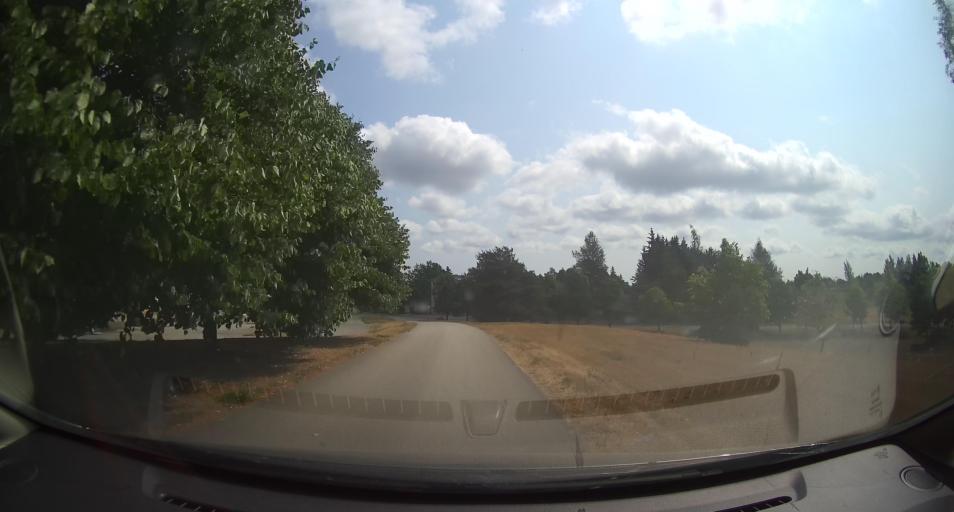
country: EE
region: Paernumaa
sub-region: Audru vald
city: Audru
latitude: 58.5143
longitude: 24.3654
